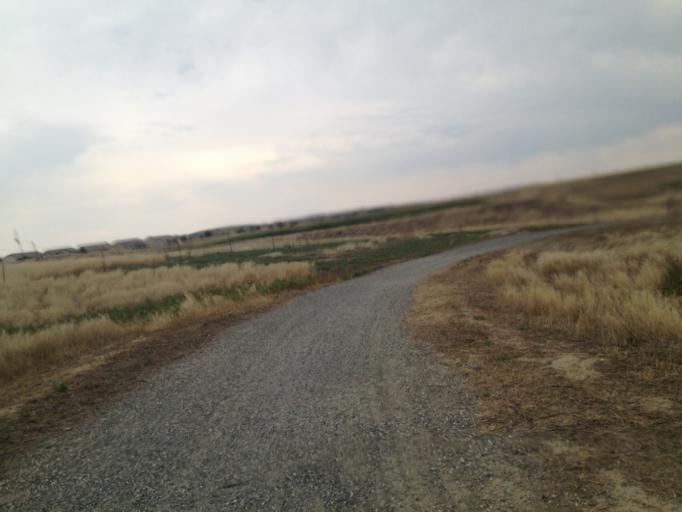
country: US
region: Colorado
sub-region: Boulder County
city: Lafayette
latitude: 39.9950
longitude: -105.0552
